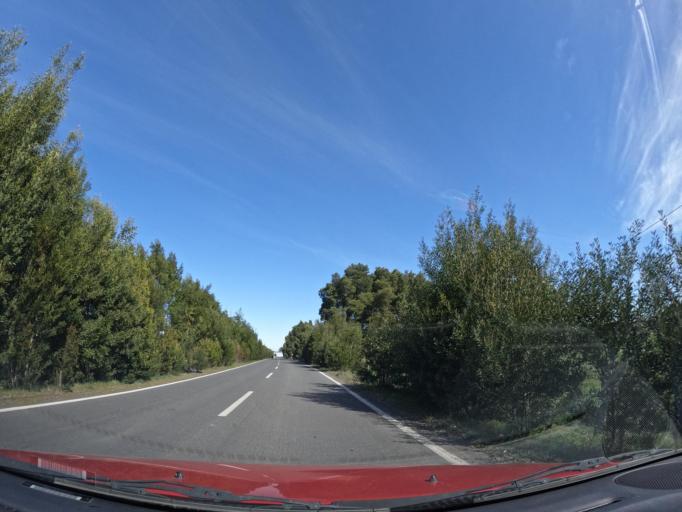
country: CL
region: Biobio
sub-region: Provincia de Biobio
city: Cabrero
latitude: -37.0359
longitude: -72.3721
